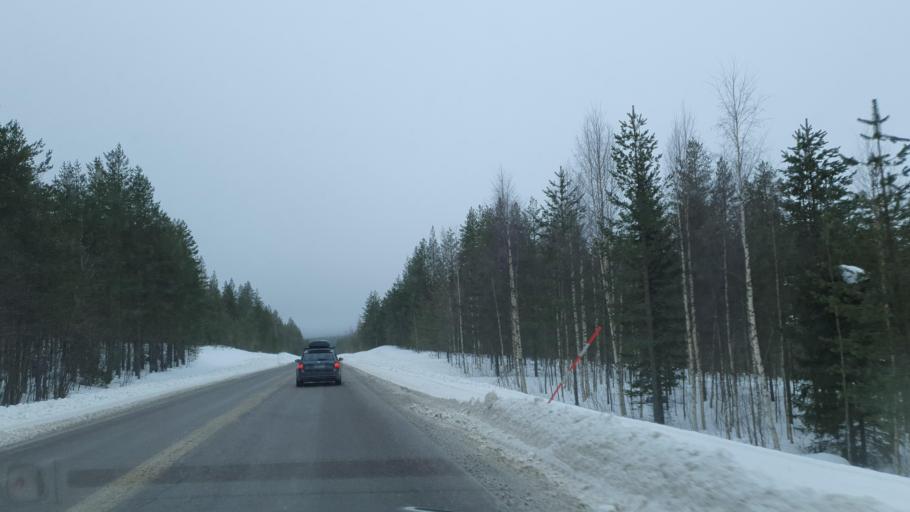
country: FI
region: Lapland
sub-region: Torniolaakso
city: Pello
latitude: 66.8596
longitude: 24.0475
